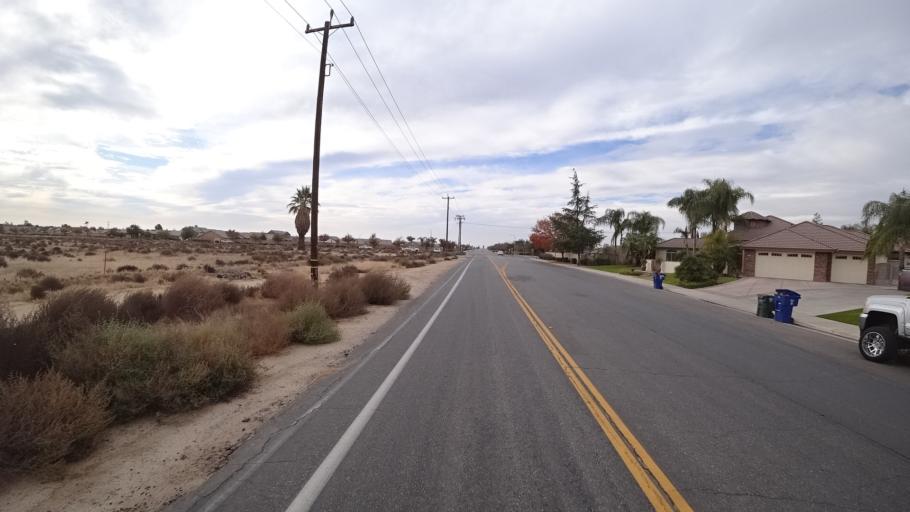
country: US
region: California
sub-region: Kern County
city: Rosedale
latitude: 35.4124
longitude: -119.1441
